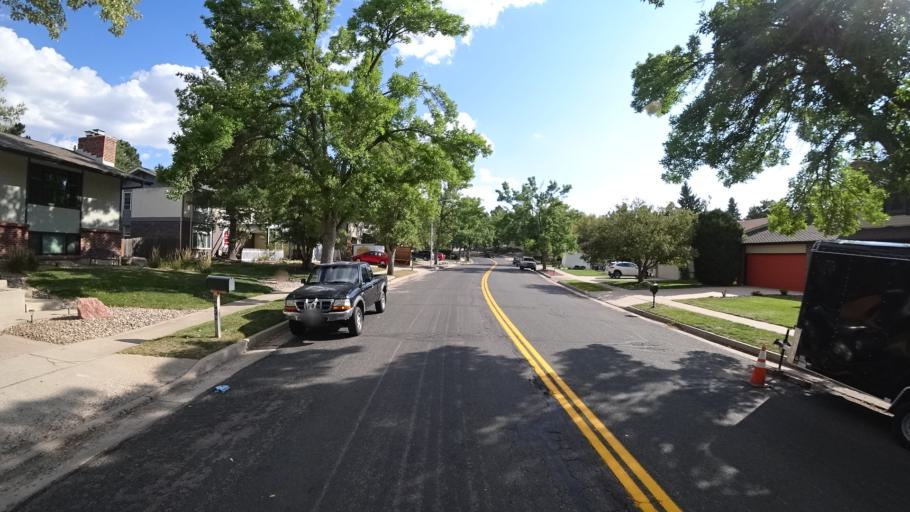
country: US
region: Colorado
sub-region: El Paso County
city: Cimarron Hills
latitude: 38.8746
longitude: -104.7393
